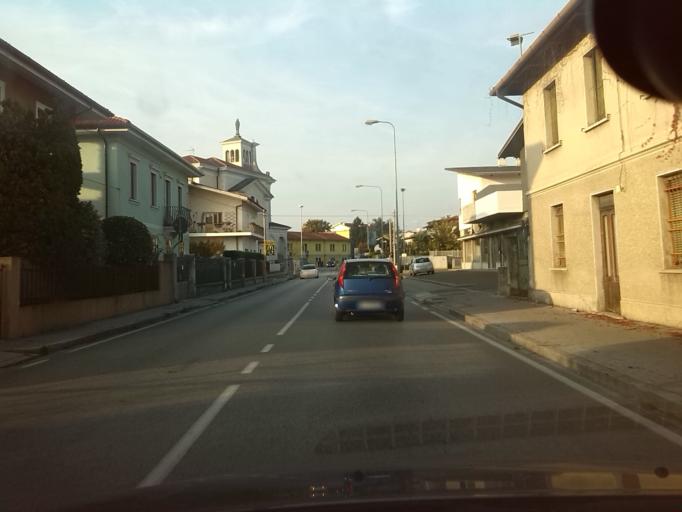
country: IT
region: Friuli Venezia Giulia
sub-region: Provincia di Udine
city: Basaldella
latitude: 46.0439
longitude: 13.2210
